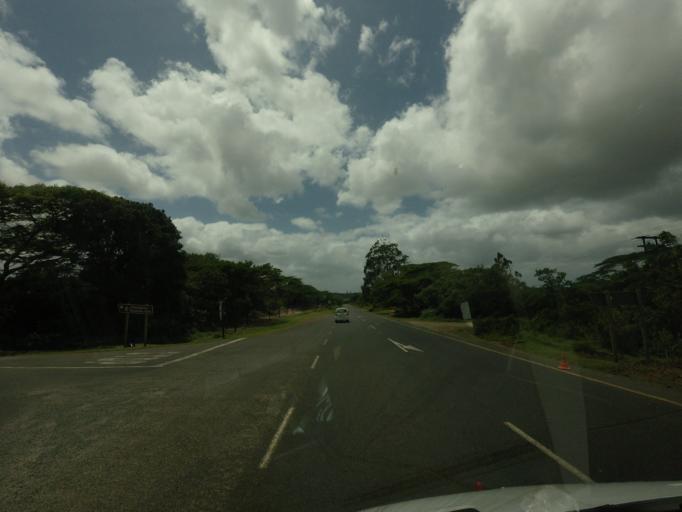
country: ZA
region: KwaZulu-Natal
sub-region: uMkhanyakude District Municipality
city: Mtubatuba
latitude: -28.3741
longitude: 32.3916
